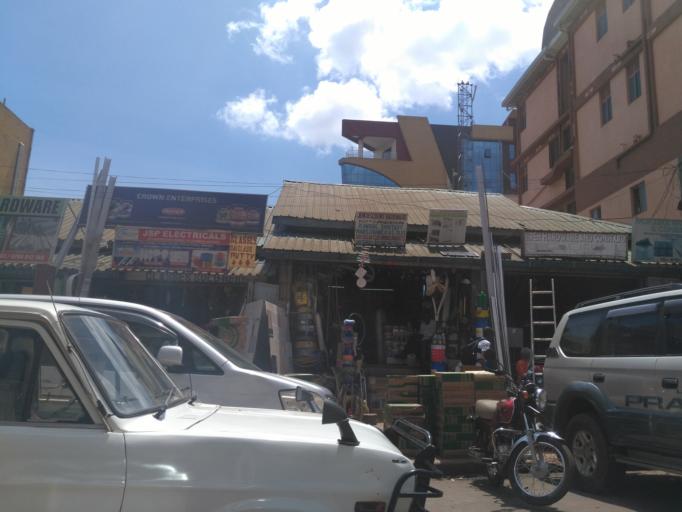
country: UG
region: Central Region
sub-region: Kampala District
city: Kampala
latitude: 0.3114
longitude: 32.5808
